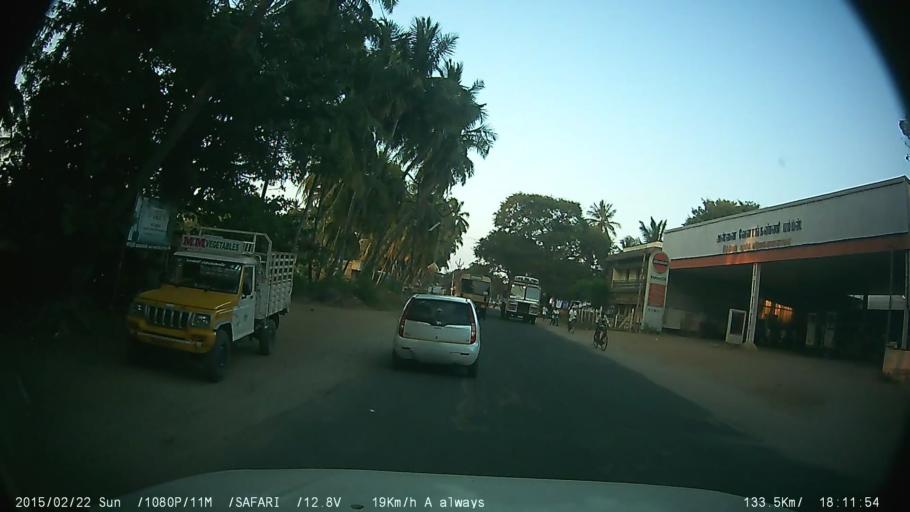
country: IN
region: Tamil Nadu
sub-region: Theni
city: Chinnamanur
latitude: 9.8454
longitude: 77.3811
